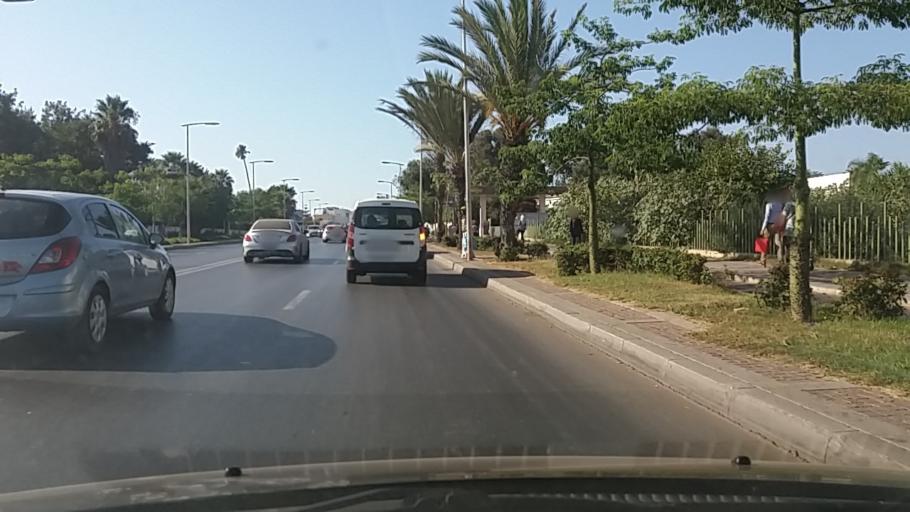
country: MA
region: Rabat-Sale-Zemmour-Zaer
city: Sale
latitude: 34.0424
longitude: -6.8169
